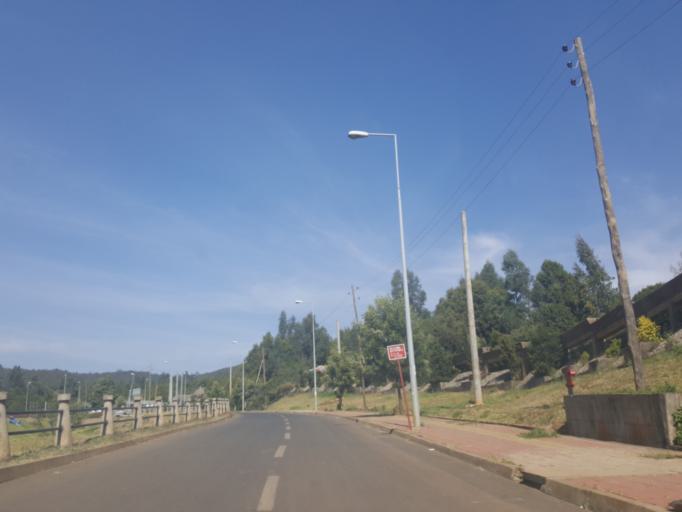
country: ET
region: Adis Abeba
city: Addis Ababa
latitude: 9.0697
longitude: 38.7231
